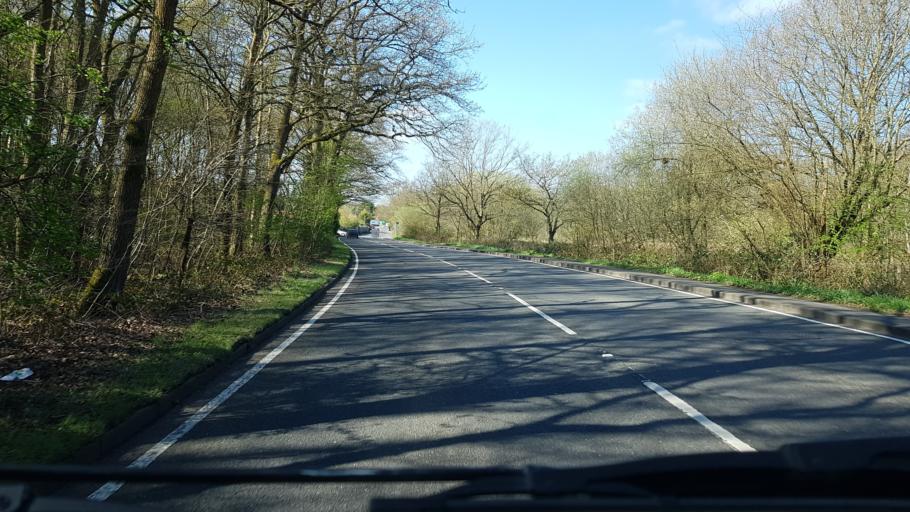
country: GB
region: England
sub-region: Surrey
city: Knaphill
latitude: 51.3071
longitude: -0.6207
